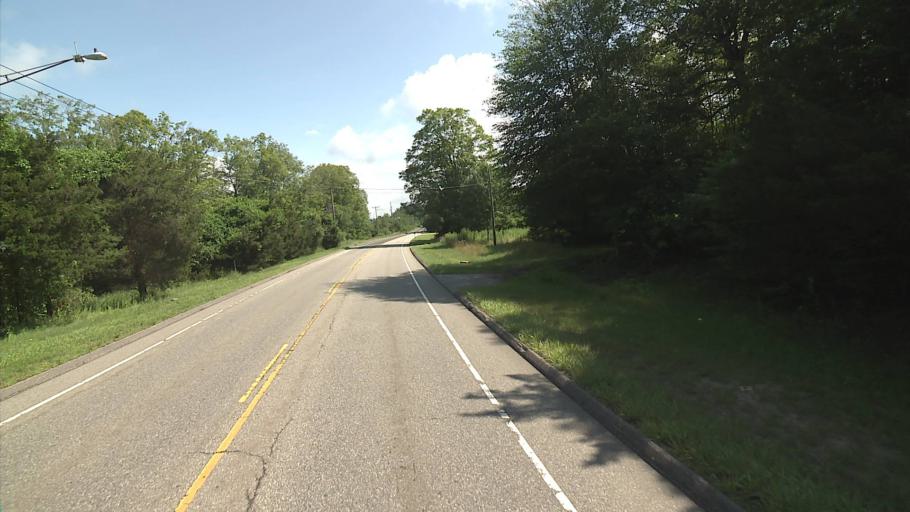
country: US
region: Connecticut
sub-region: Middlesex County
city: Westbrook Center
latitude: 41.3172
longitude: -72.4332
